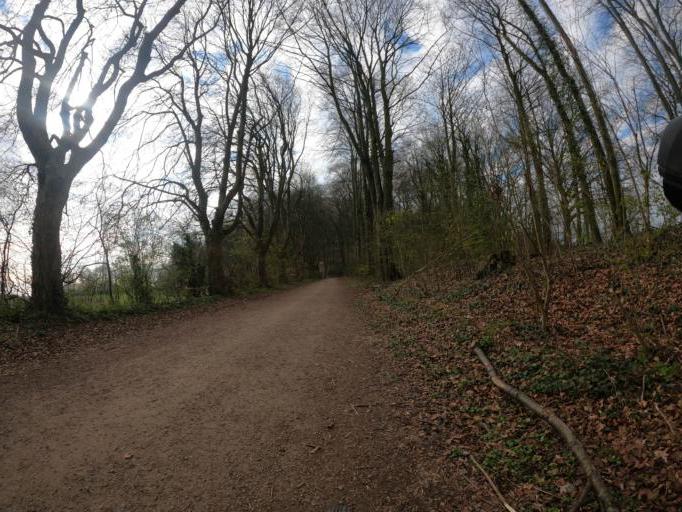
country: NL
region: Limburg
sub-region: Gemeente Vaals
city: Vaals
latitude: 50.7614
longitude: 6.0422
